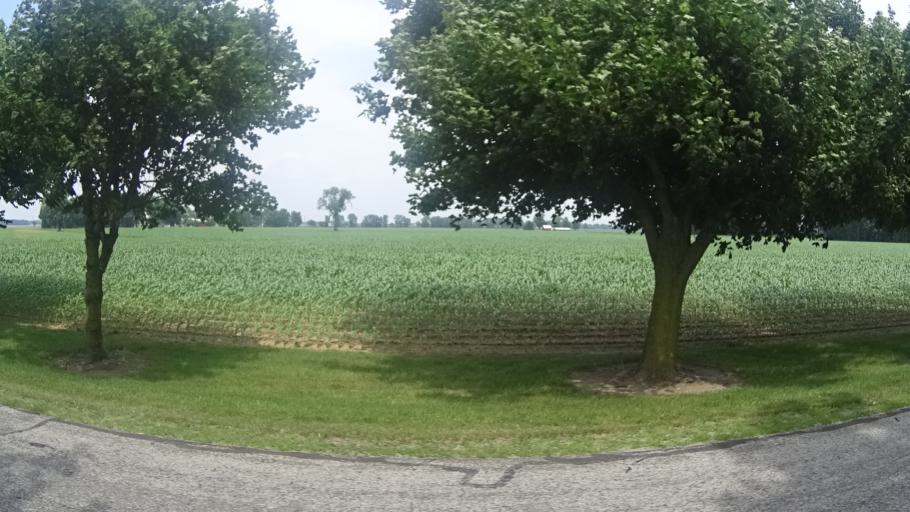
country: US
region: Ohio
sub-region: Erie County
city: Milan
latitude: 41.3120
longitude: -82.6661
